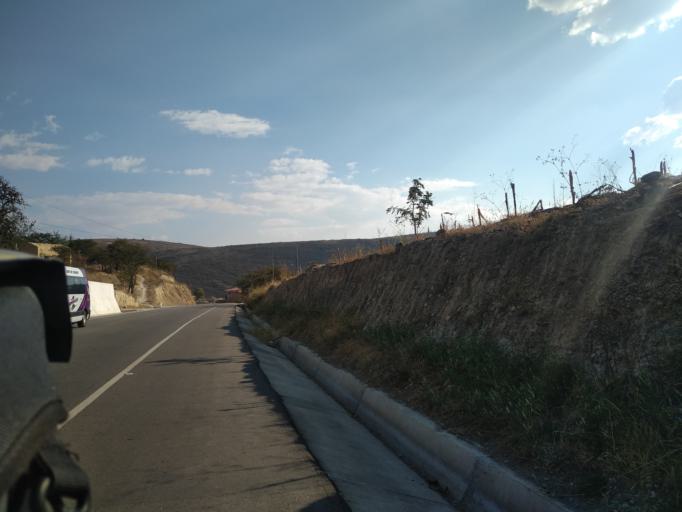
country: PE
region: Cajamarca
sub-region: San Marcos
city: San Marcos
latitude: -7.3691
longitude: -78.1281
